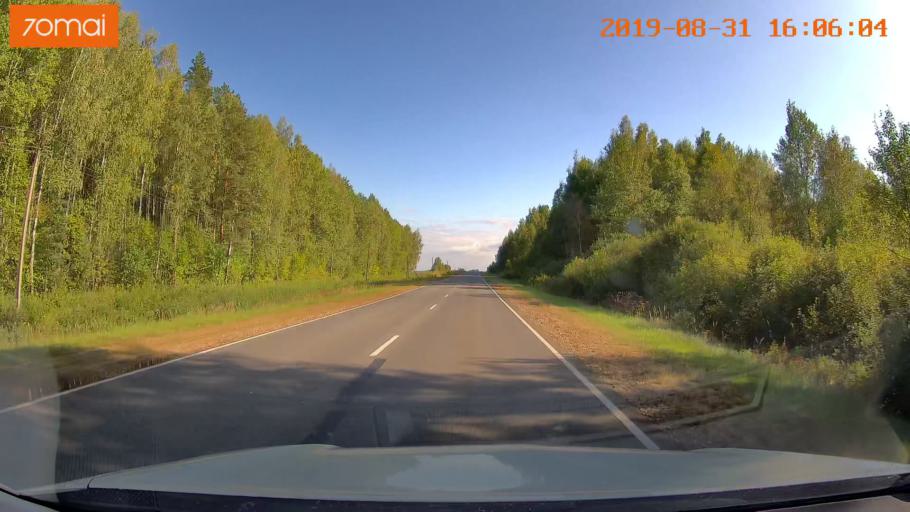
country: RU
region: Kaluga
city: Yukhnov
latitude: 54.6297
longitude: 35.3421
